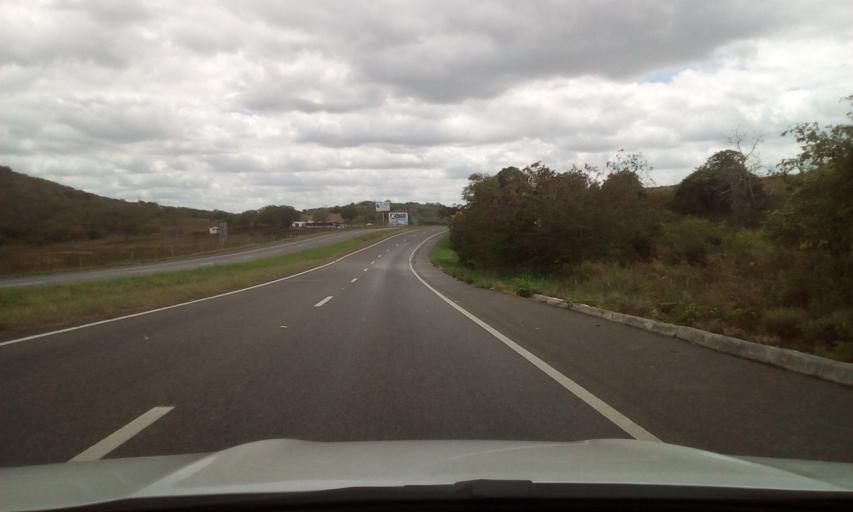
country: BR
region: Paraiba
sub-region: Massaranduba
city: Massaranduba
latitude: -7.2663
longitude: -35.7191
